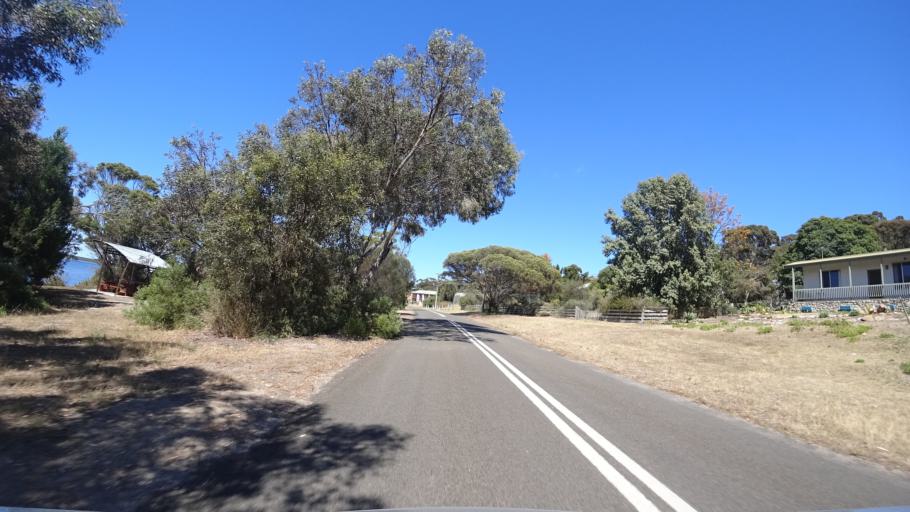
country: AU
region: South Australia
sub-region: Kangaroo Island
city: Kingscote
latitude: -35.7746
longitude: 137.7788
